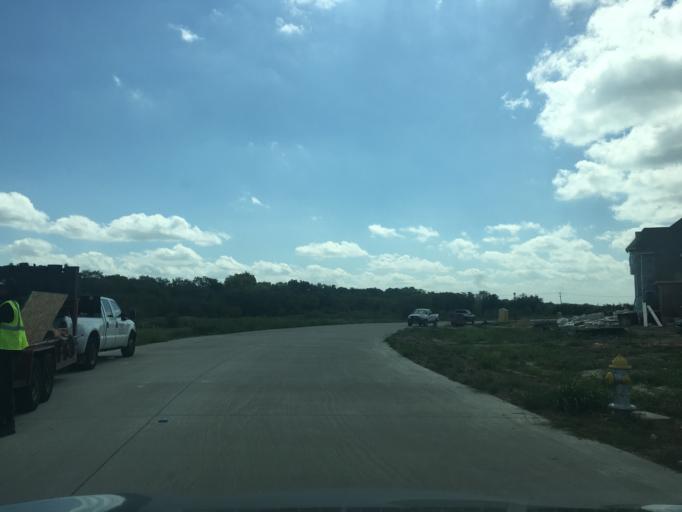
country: US
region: Texas
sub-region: Dallas County
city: Sachse
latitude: 32.9687
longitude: -96.5545
